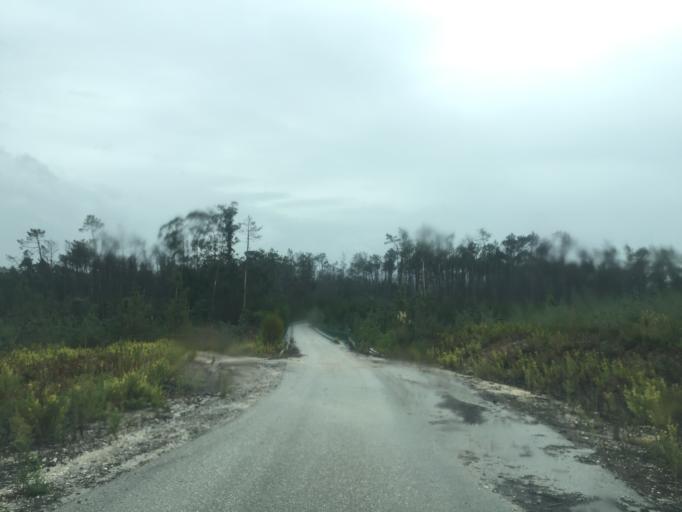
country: PT
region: Coimbra
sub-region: Figueira da Foz
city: Lavos
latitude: 40.0718
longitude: -8.7849
